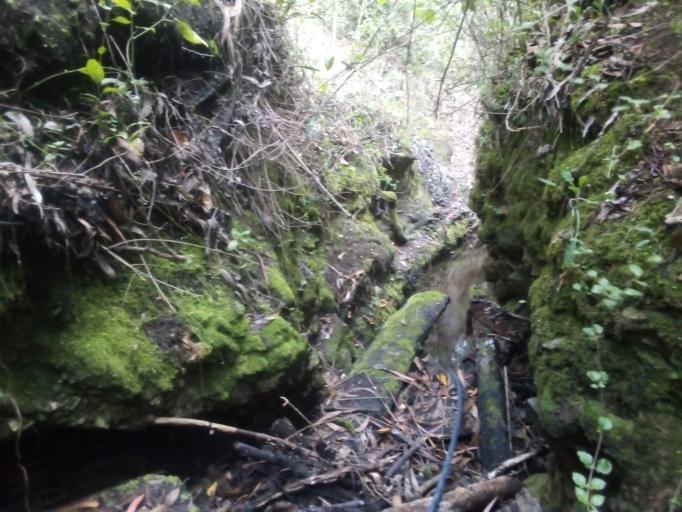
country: CO
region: Boyaca
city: Tuta
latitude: 5.6633
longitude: -73.1769
